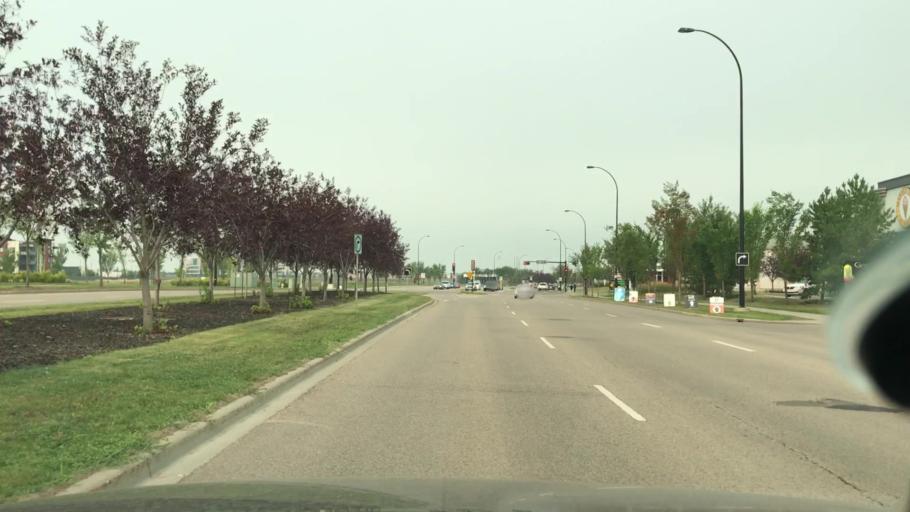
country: CA
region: Alberta
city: Devon
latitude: 53.4348
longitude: -113.6057
